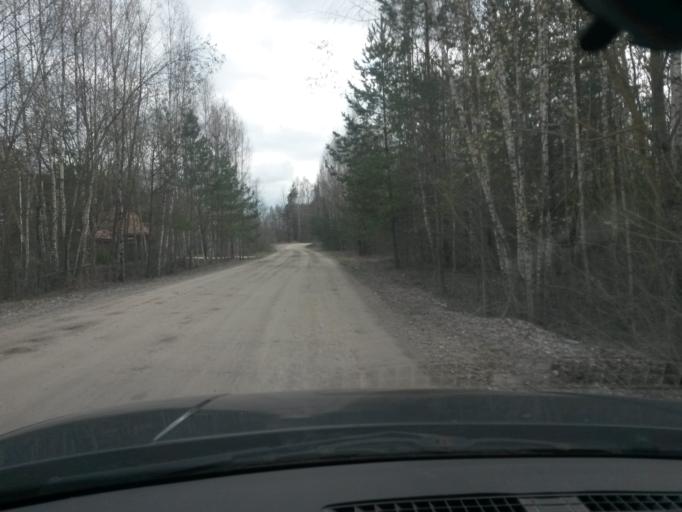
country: LV
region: Stopini
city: Ulbroka
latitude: 56.8950
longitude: 24.2476
